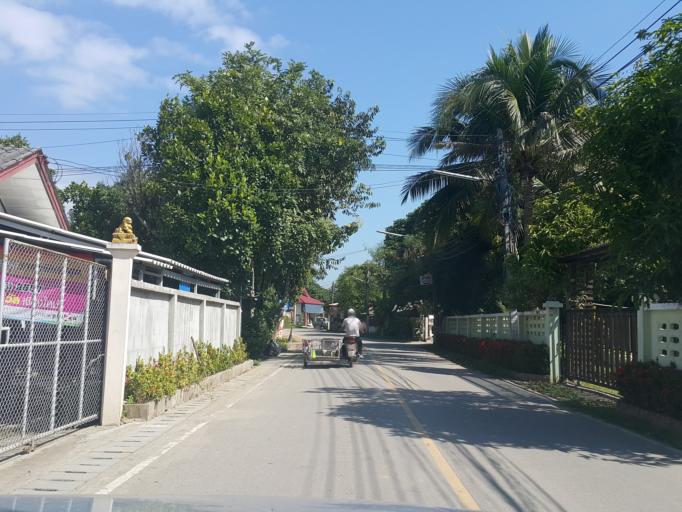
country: TH
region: Chiang Mai
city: Saraphi
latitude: 18.7507
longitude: 99.0513
